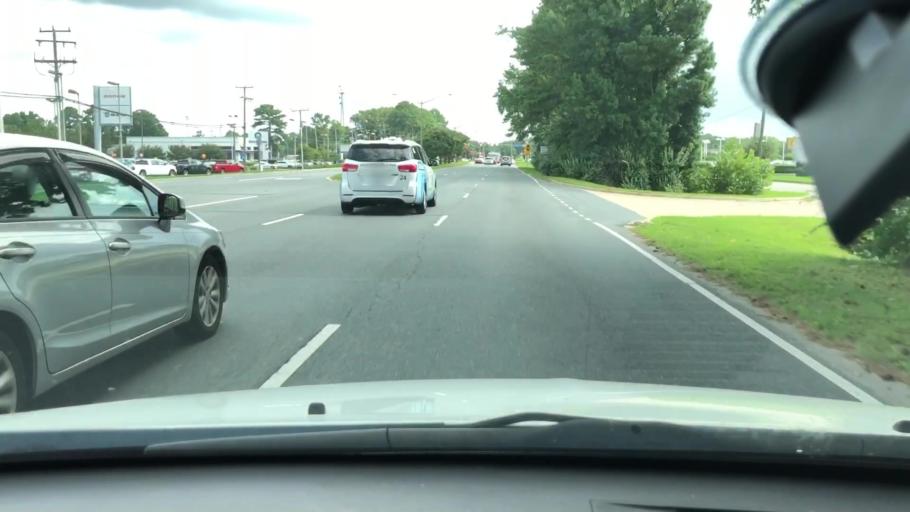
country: US
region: Virginia
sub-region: City of Chesapeake
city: Chesapeake
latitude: 36.7918
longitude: -76.2434
